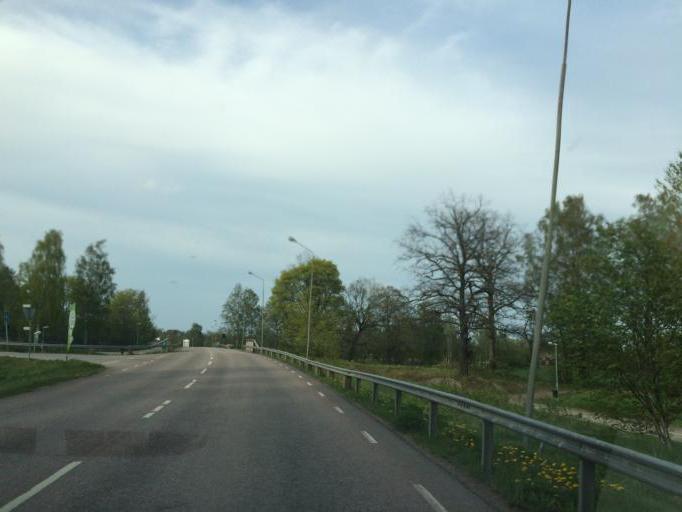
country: SE
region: Vaestmanland
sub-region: Hallstahammars Kommun
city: Hallstahammar
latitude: 59.6074
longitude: 16.2146
